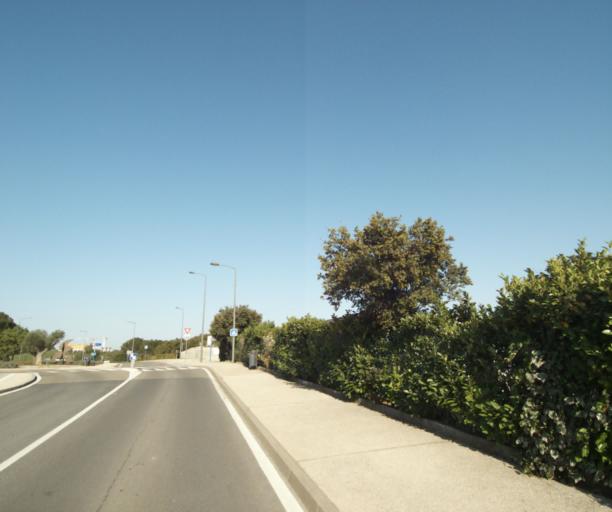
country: FR
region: Languedoc-Roussillon
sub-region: Departement de l'Herault
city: Jacou
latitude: 43.6451
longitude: 3.9173
